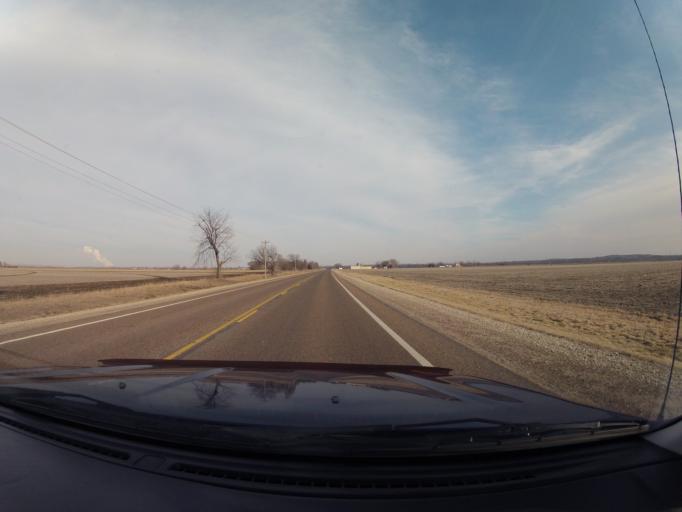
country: US
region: Kansas
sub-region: Pottawatomie County
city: Wamego
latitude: 39.2098
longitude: -96.2766
